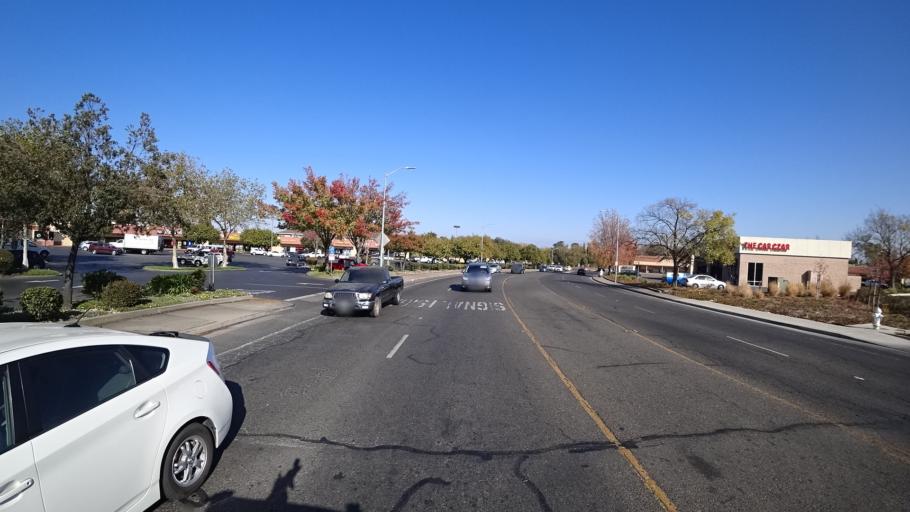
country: US
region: California
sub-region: Sacramento County
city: Citrus Heights
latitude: 38.6793
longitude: -121.2922
